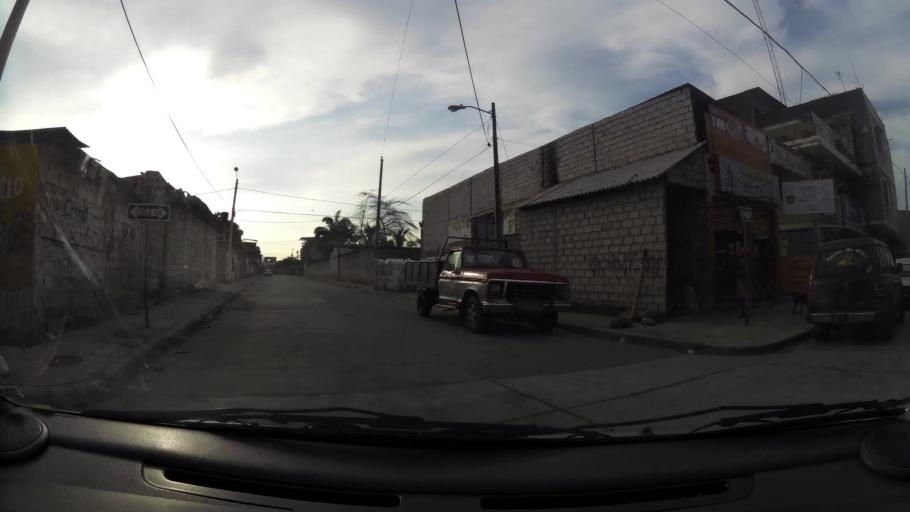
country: EC
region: Guayas
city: Eloy Alfaro
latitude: -2.0890
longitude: -79.9039
